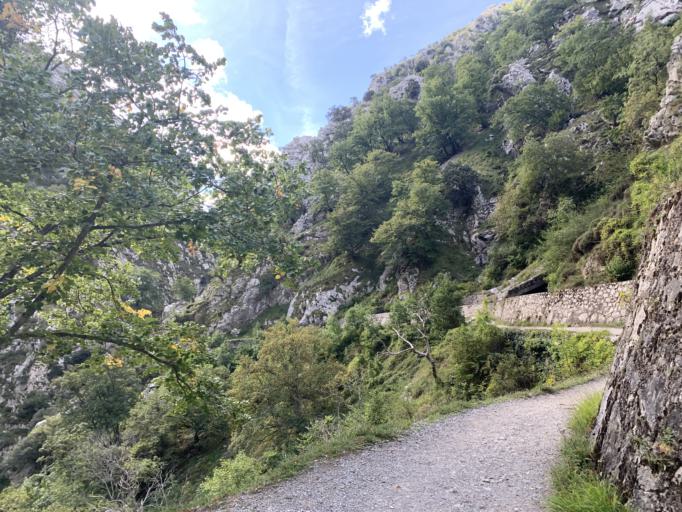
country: ES
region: Castille and Leon
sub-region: Provincia de Leon
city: Posada de Valdeon
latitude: 43.2288
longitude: -4.8943
